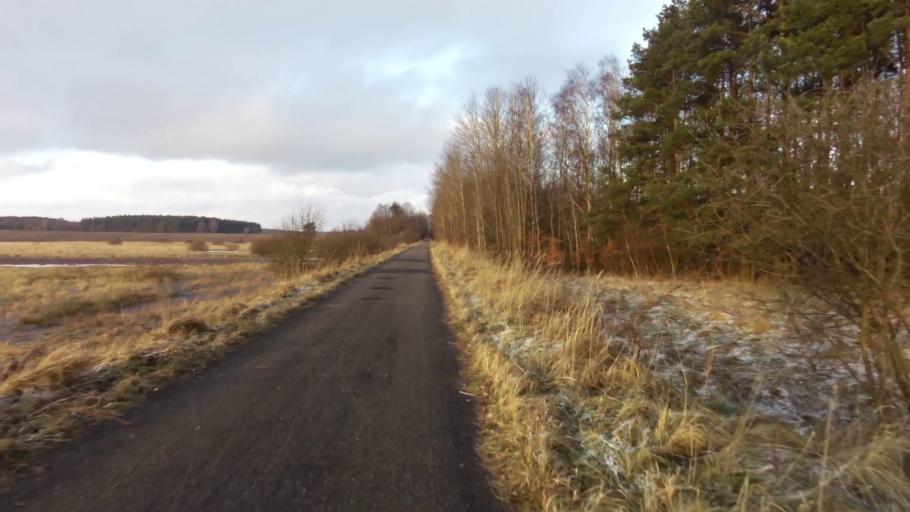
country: PL
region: West Pomeranian Voivodeship
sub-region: Powiat drawski
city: Zlocieniec
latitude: 53.6036
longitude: 16.0462
